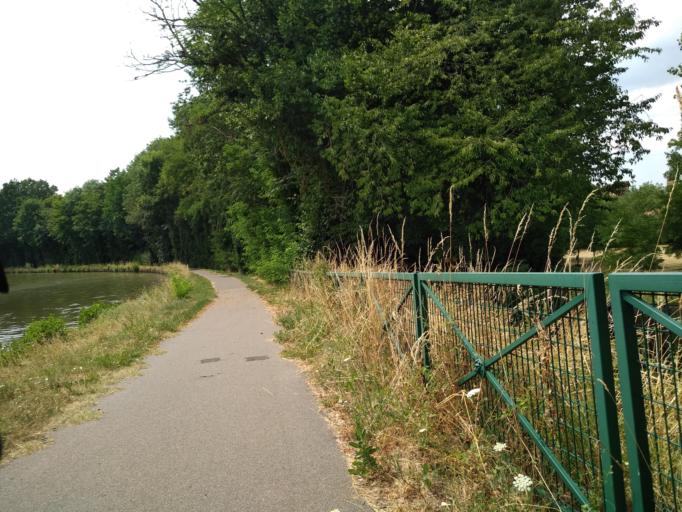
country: FR
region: Auvergne
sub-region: Departement de l'Allier
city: Diou
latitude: 46.5322
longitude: 3.7449
